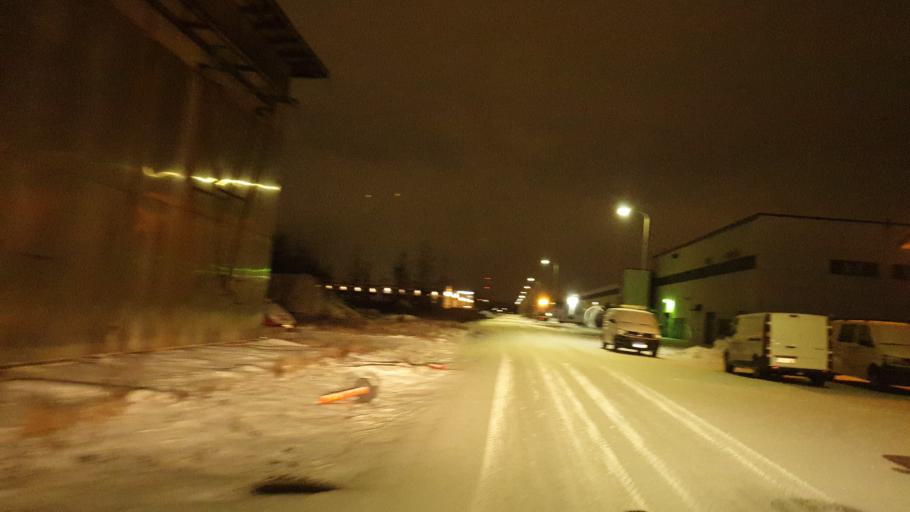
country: FI
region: Northern Ostrobothnia
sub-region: Oulu
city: Oulu
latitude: 64.9957
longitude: 25.4394
